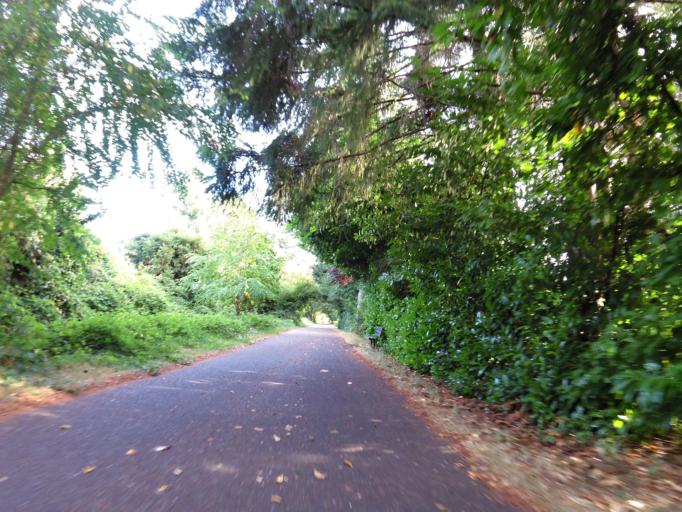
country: US
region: Washington
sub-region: Thurston County
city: Lacey
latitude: 47.0261
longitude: -122.8360
